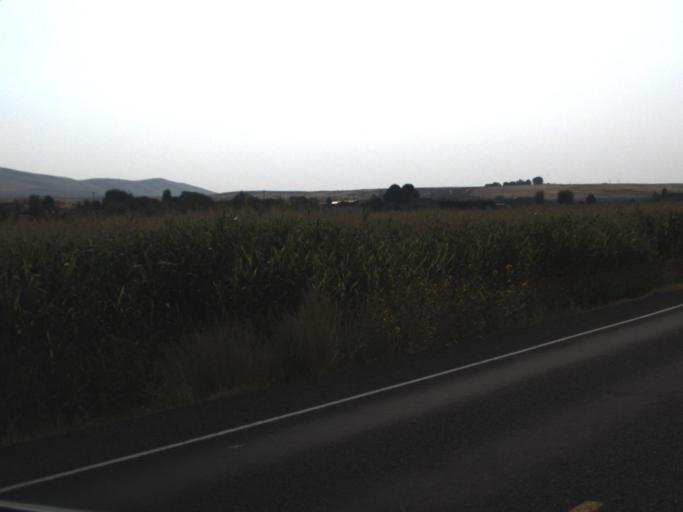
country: US
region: Washington
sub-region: Yakima County
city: Grandview
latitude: 46.1865
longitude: -119.8647
